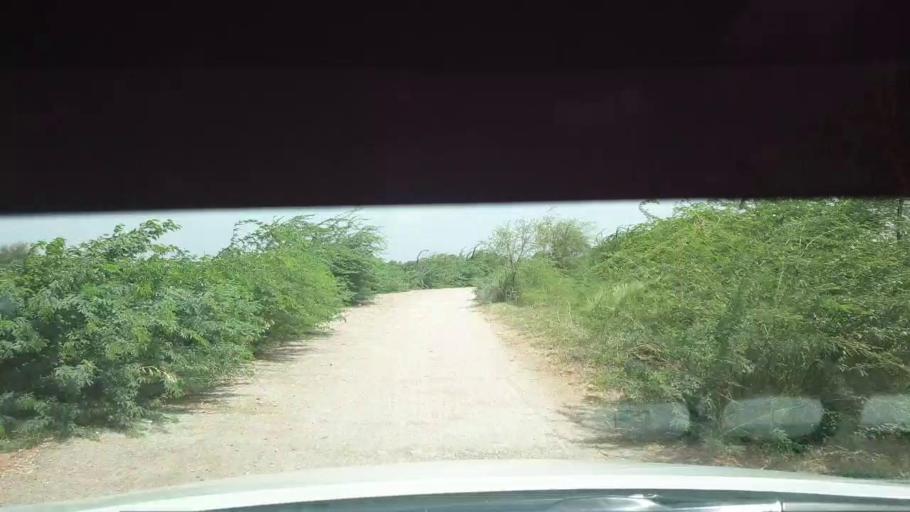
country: PK
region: Sindh
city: Kadhan
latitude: 24.5032
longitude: 68.9801
